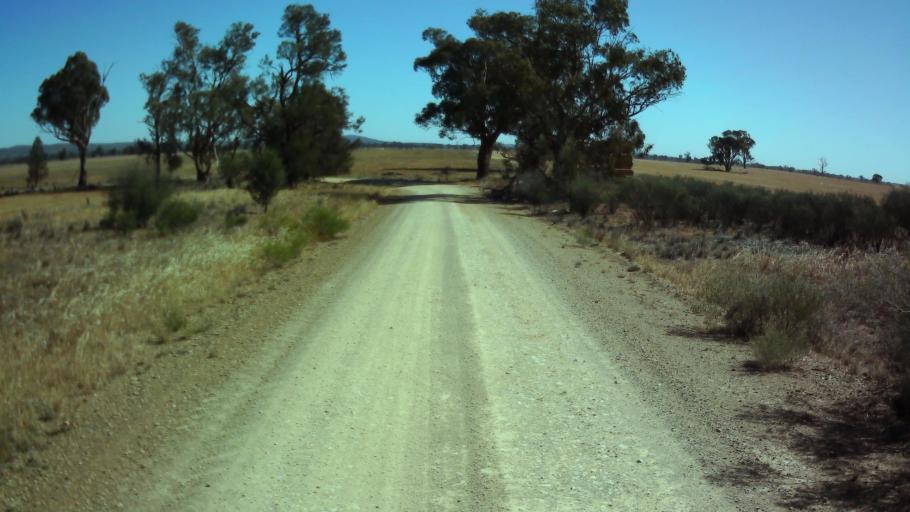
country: AU
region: New South Wales
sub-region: Weddin
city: Grenfell
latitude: -33.8745
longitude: 147.8744
